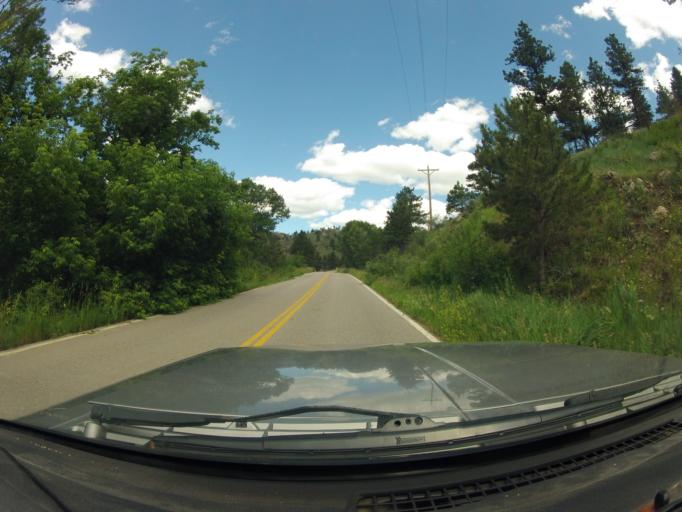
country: US
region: Colorado
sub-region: Larimer County
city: Laporte
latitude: 40.5740
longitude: -105.3246
